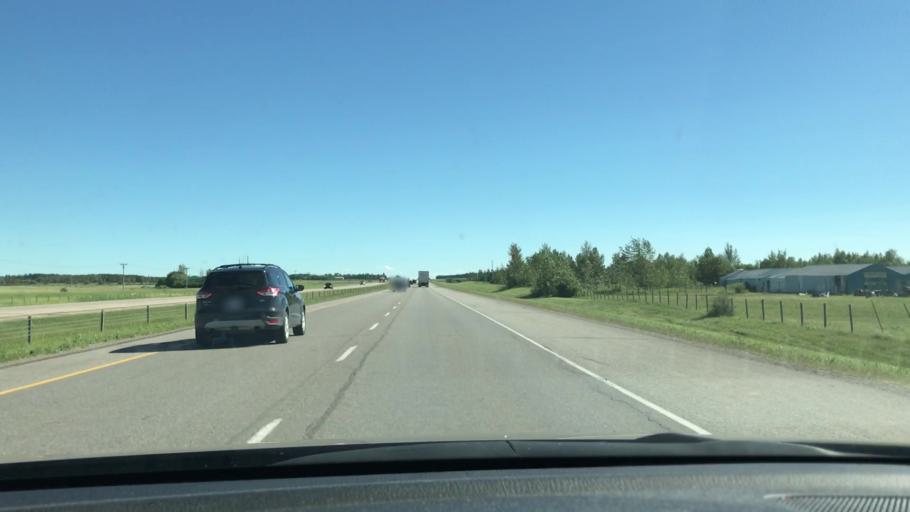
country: CA
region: Alberta
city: Olds
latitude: 51.9080
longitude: -114.0254
